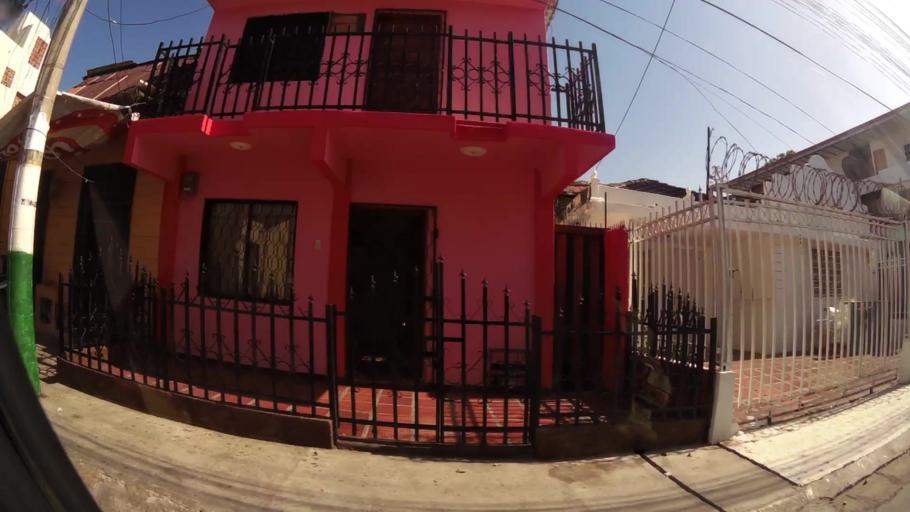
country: CO
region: Bolivar
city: Cartagena
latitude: 10.4249
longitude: -75.5372
